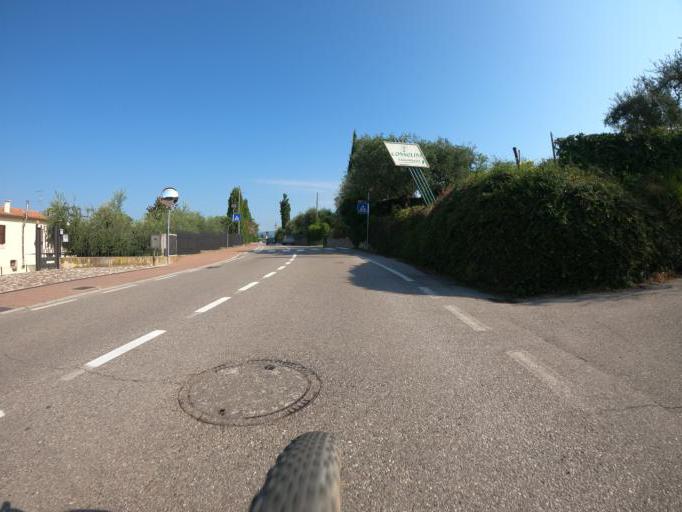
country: IT
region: Veneto
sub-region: Provincia di Verona
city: Bardolino
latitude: 45.5371
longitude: 10.7348
